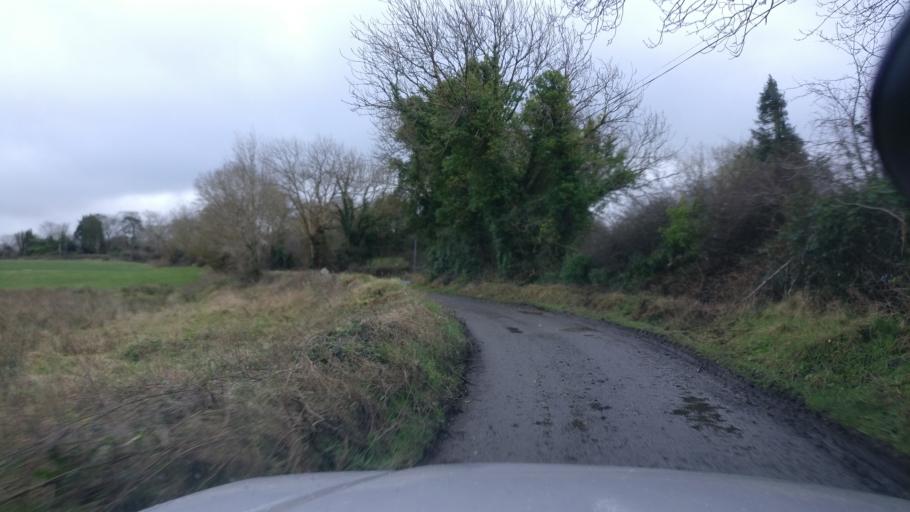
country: IE
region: Connaught
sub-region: County Galway
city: Athenry
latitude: 53.2110
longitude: -8.6975
